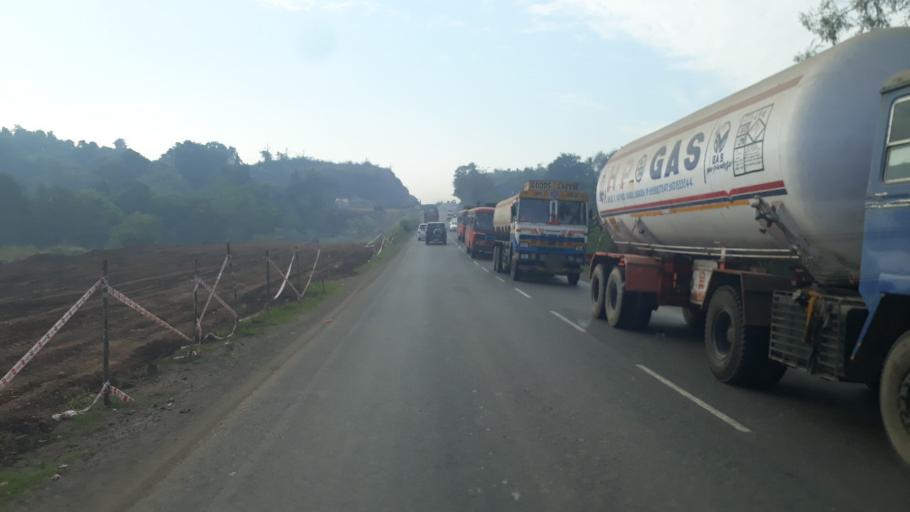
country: IN
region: Maharashtra
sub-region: Raigarh
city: Pen
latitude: 18.8302
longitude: 73.0938
